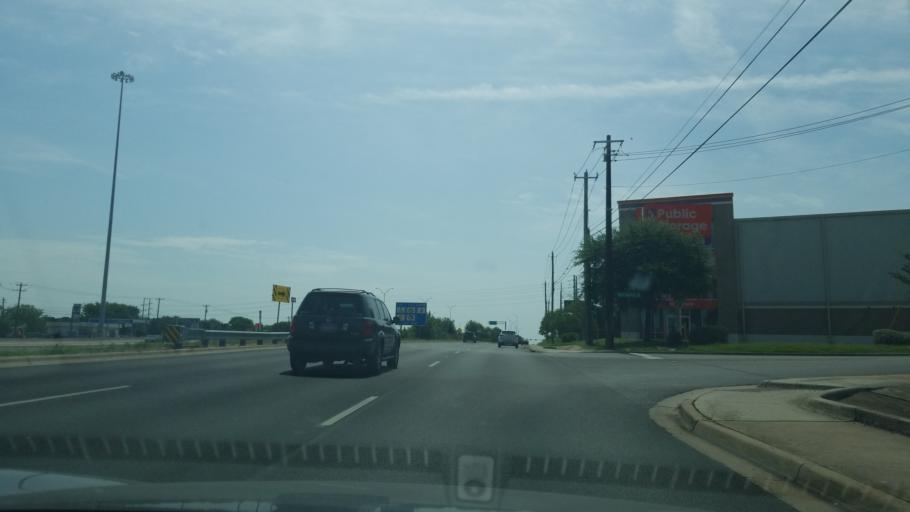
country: US
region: Texas
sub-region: Travis County
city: Austin
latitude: 30.2156
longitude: -97.7404
